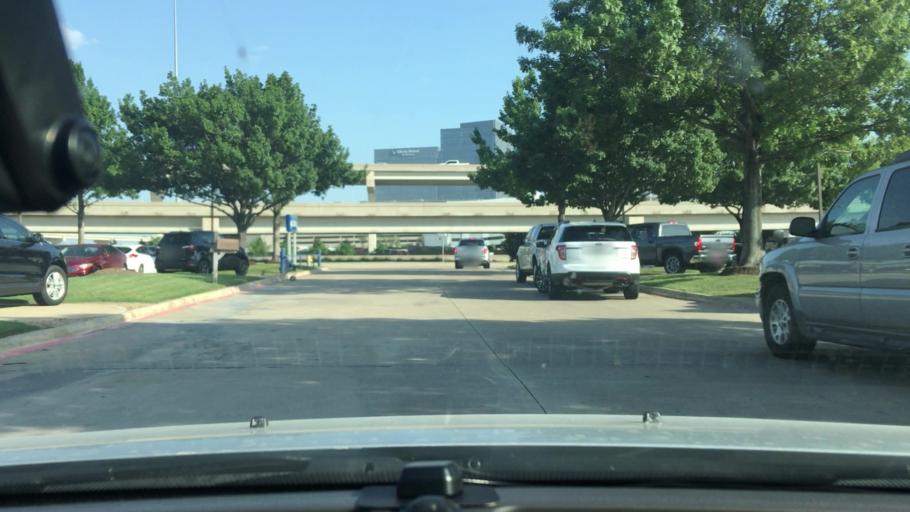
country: US
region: Texas
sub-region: Denton County
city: The Colony
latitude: 33.0910
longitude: -96.8273
